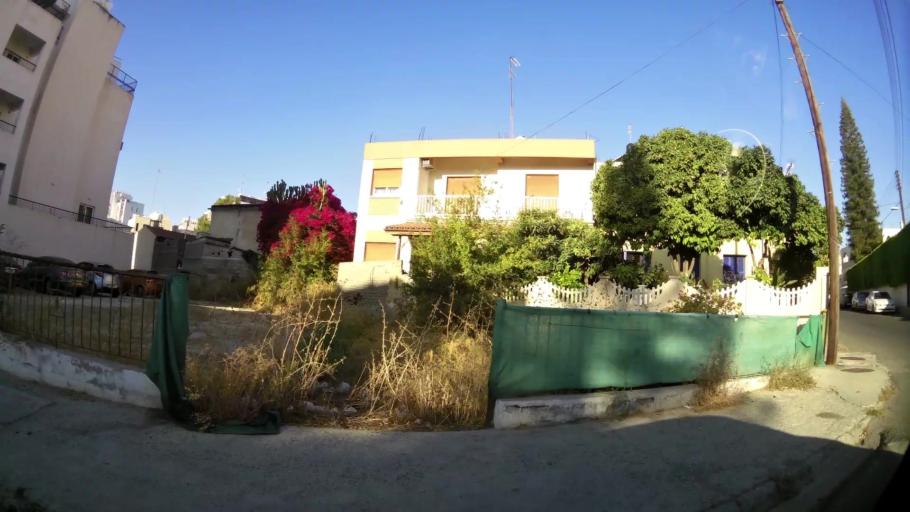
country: CY
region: Larnaka
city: Larnaca
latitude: 34.9155
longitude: 33.6303
